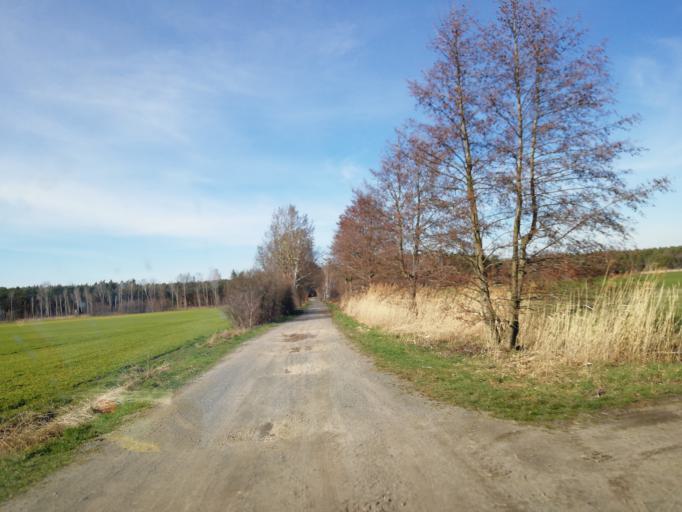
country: DE
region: Brandenburg
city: Ruckersdorf
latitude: 51.5589
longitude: 13.5922
